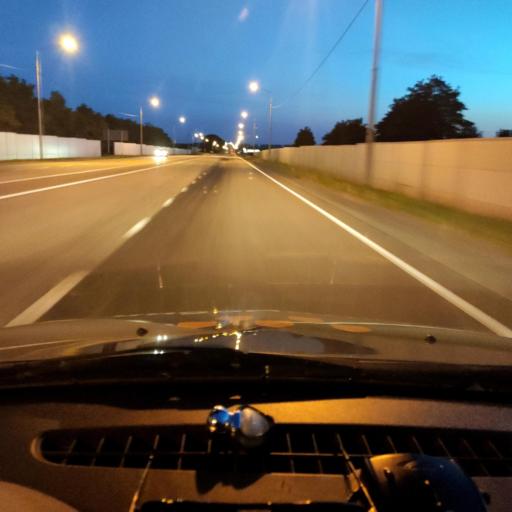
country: RU
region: Belgorod
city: Skorodnoye
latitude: 51.1851
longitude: 37.3604
